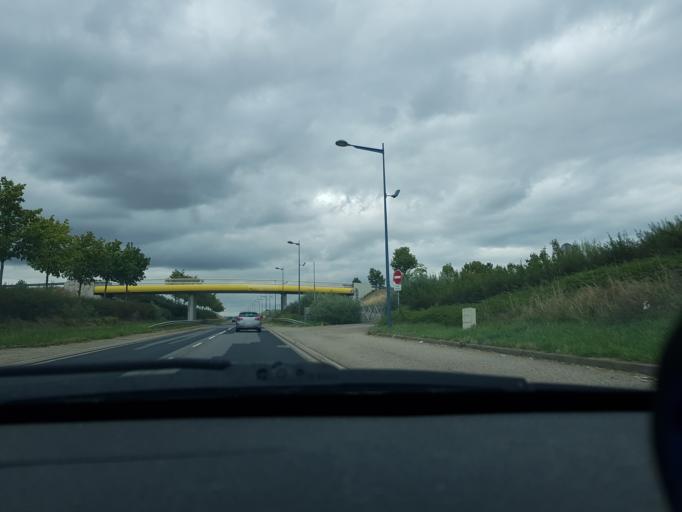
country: FR
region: Lorraine
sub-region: Departement de Meurthe-et-Moselle
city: Saulxures-les-Nancy
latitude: 48.6923
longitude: 6.2393
